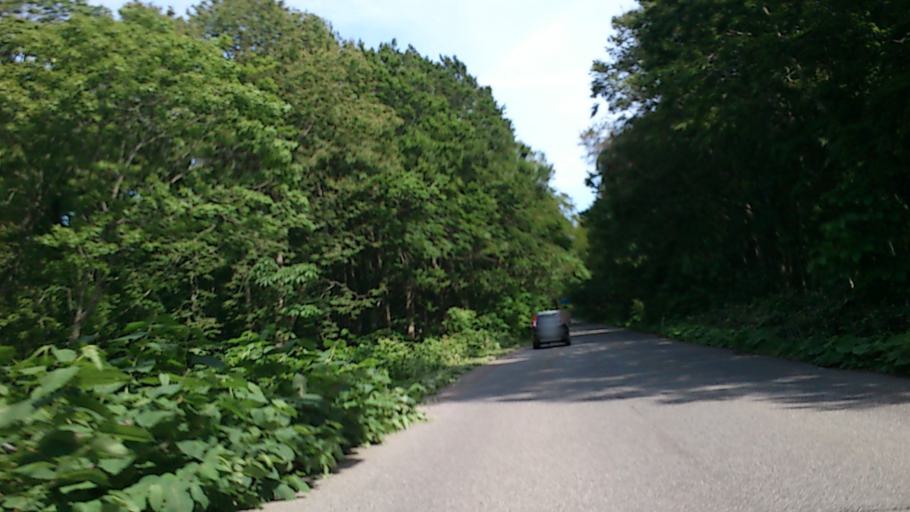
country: JP
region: Aomori
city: Aomori Shi
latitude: 40.6995
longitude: 140.8338
